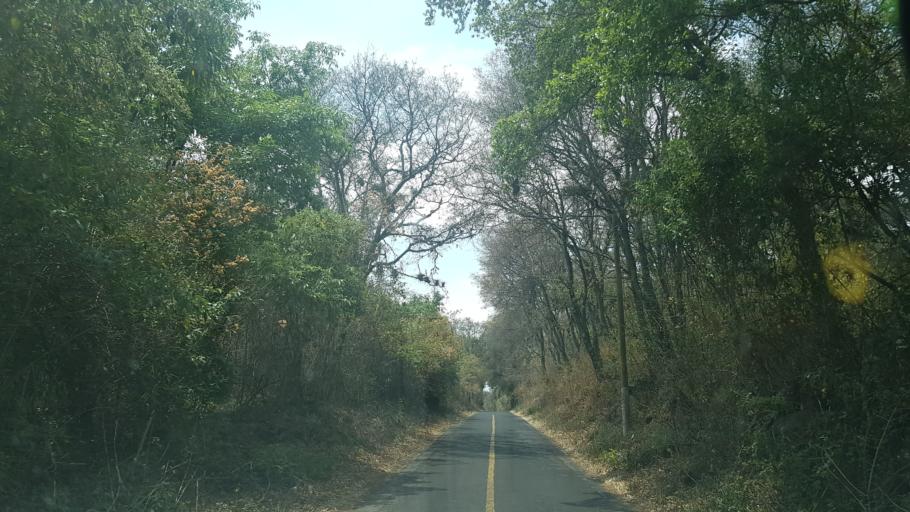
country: MX
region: Puebla
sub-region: Tochimilco
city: La Magdalena Yancuitlalpan
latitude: 18.8806
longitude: -98.5966
